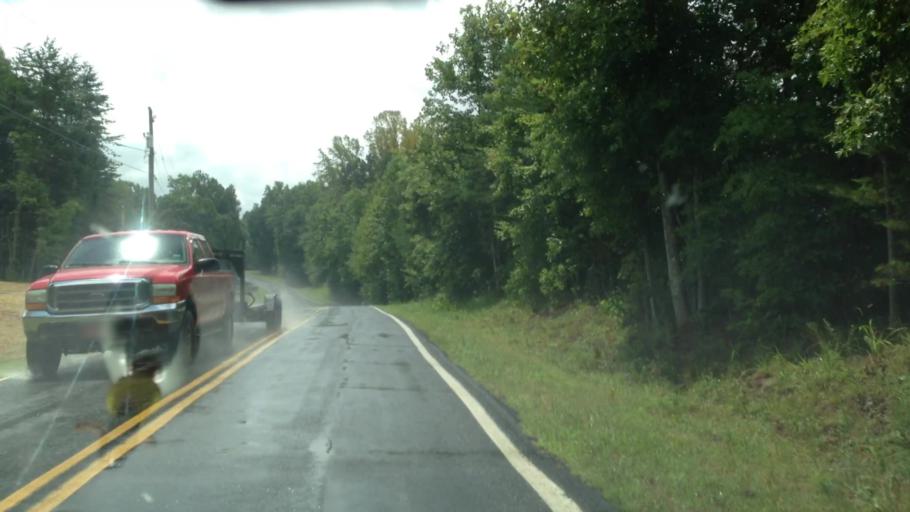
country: US
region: North Carolina
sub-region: Forsyth County
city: Walkertown
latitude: 36.2075
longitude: -80.1090
